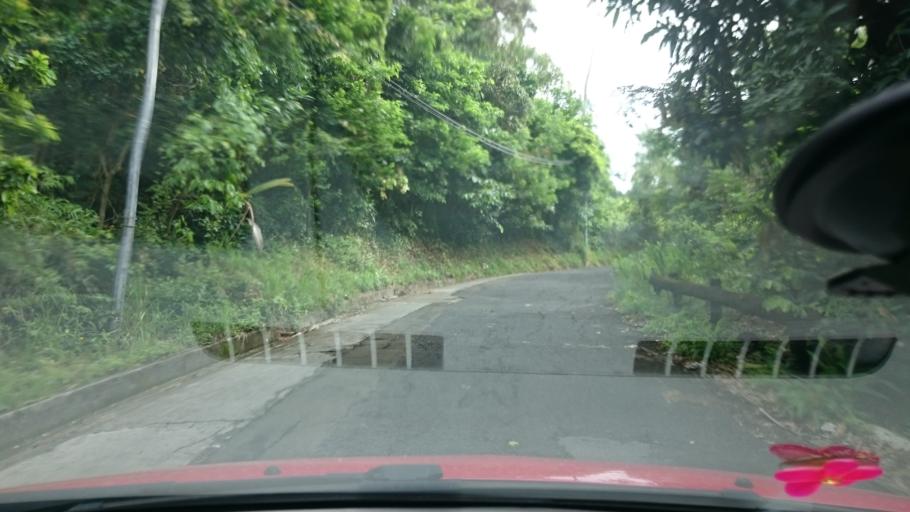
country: MQ
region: Martinique
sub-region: Martinique
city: Riviere-Pilote
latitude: 14.4893
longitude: -60.9086
